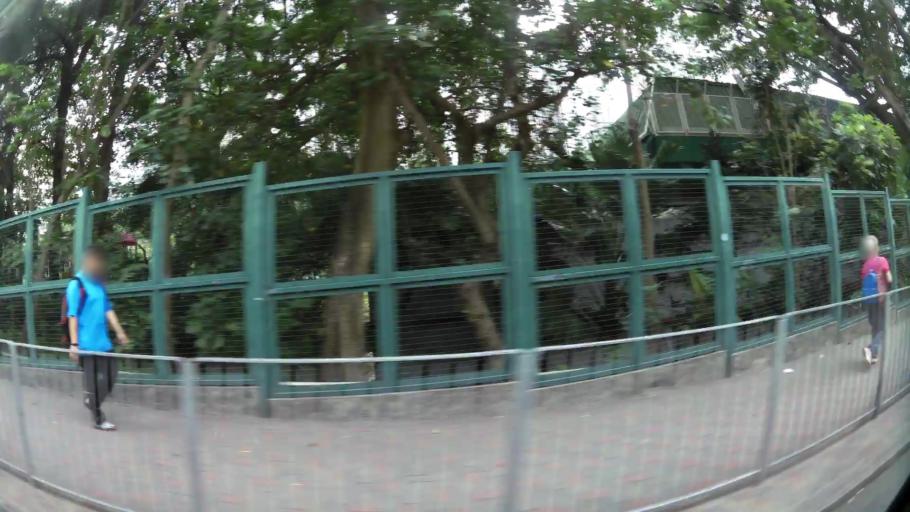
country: HK
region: Kowloon City
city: Kowloon
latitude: 22.3199
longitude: 114.2273
